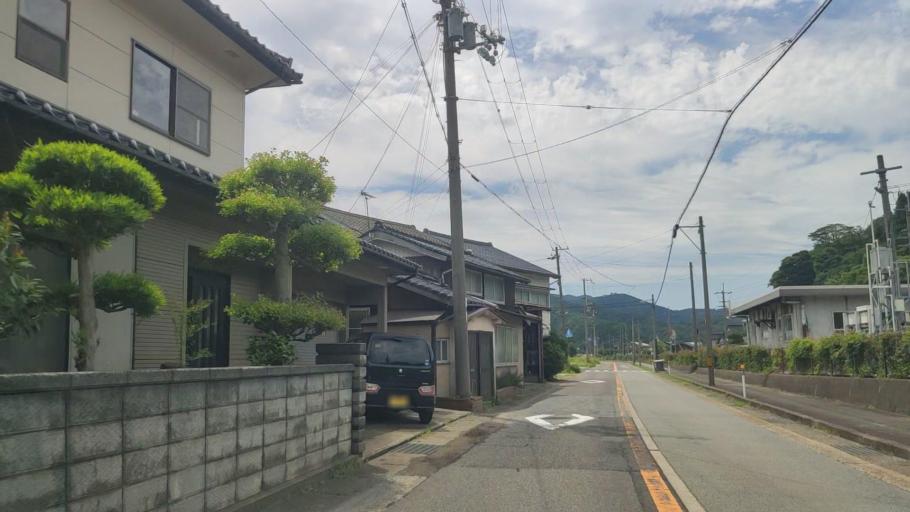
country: JP
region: Hyogo
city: Toyooka
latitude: 35.6493
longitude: 134.7573
